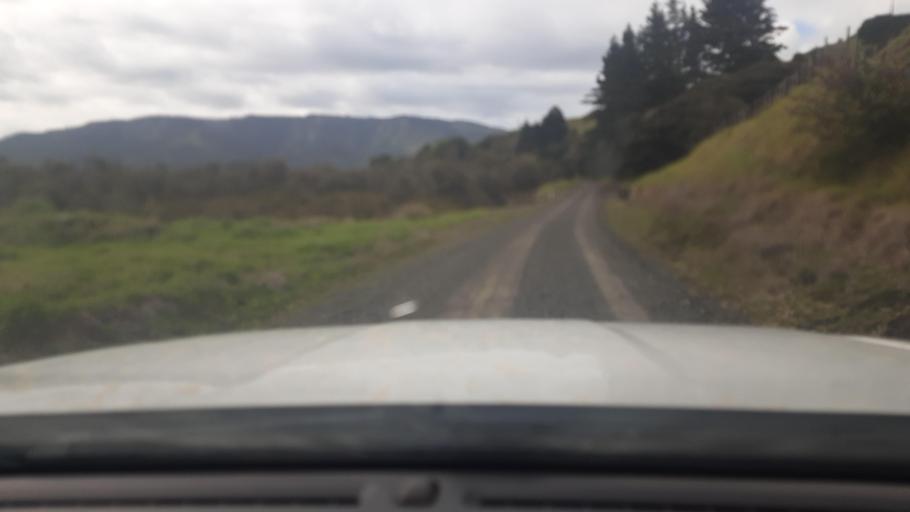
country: NZ
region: Northland
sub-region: Far North District
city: Ahipara
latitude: -35.3370
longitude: 173.2239
